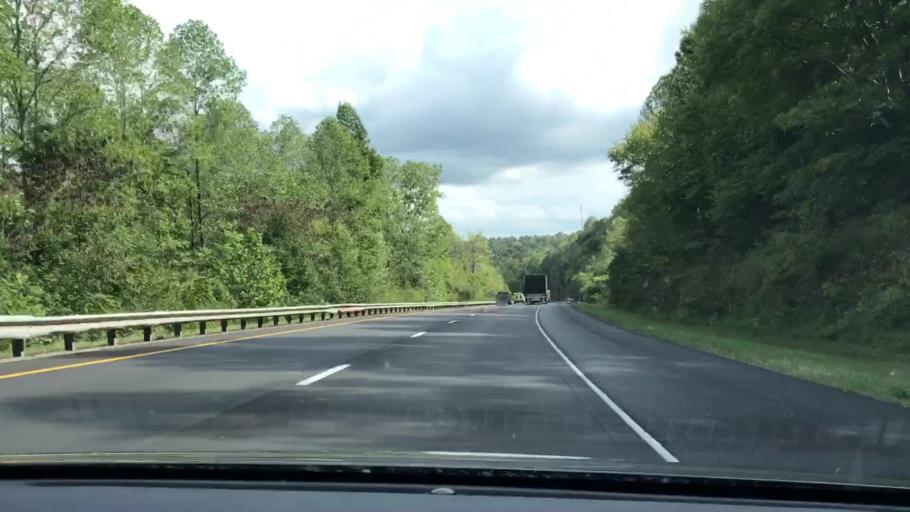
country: US
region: Tennessee
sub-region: Robertson County
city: Ridgetop
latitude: 36.3204
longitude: -86.8509
